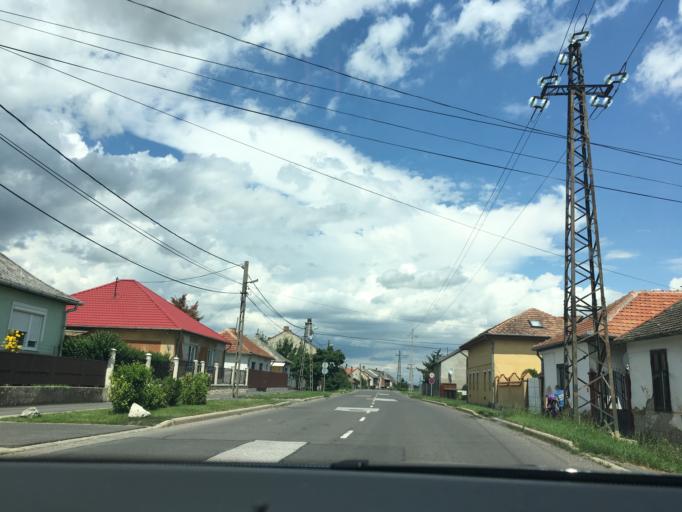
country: HU
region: Borsod-Abauj-Zemplen
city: Satoraljaujhely
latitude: 48.4029
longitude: 21.6624
